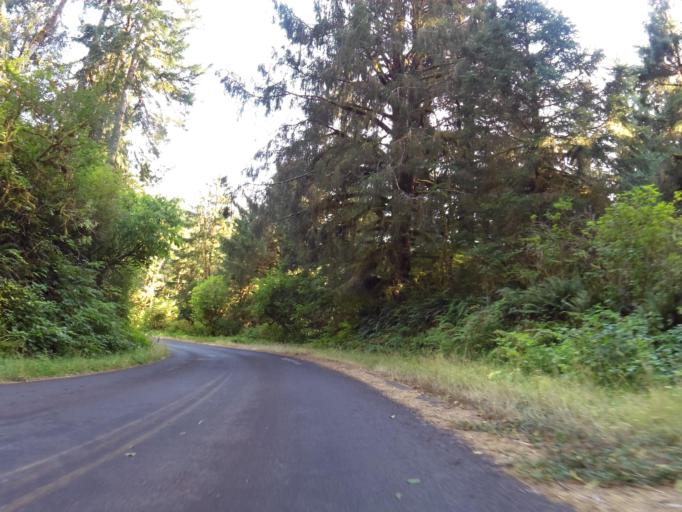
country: US
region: Oregon
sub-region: Lincoln County
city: Rose Lodge
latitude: 45.0403
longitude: -123.9126
